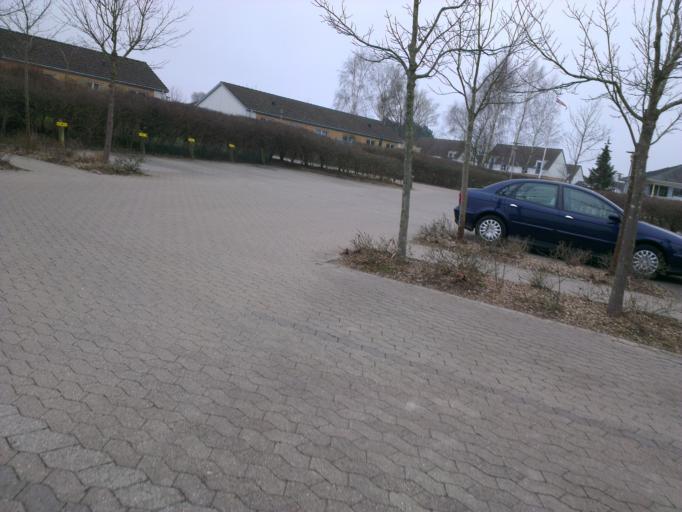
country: DK
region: Capital Region
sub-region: Frederikssund Kommune
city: Frederikssund
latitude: 55.8183
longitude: 12.0188
